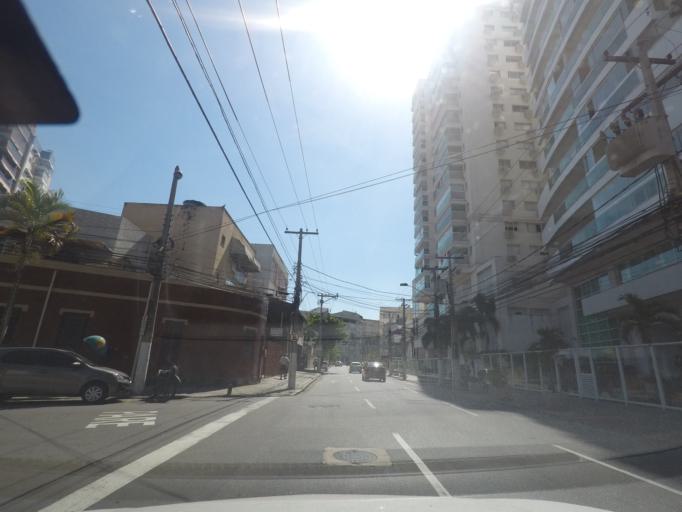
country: BR
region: Rio de Janeiro
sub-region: Niteroi
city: Niteroi
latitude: -22.8993
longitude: -43.1077
